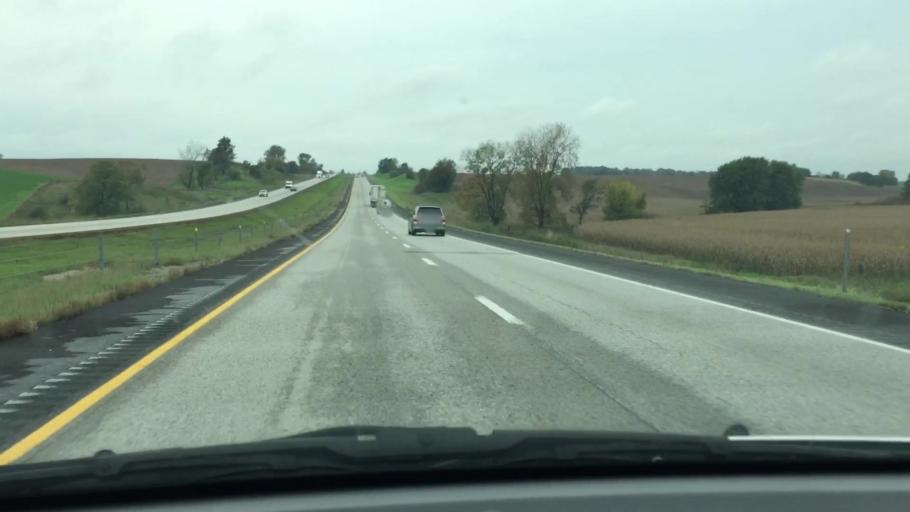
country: US
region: Iowa
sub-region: Johnson County
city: Tiffin
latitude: 41.6955
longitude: -91.7223
